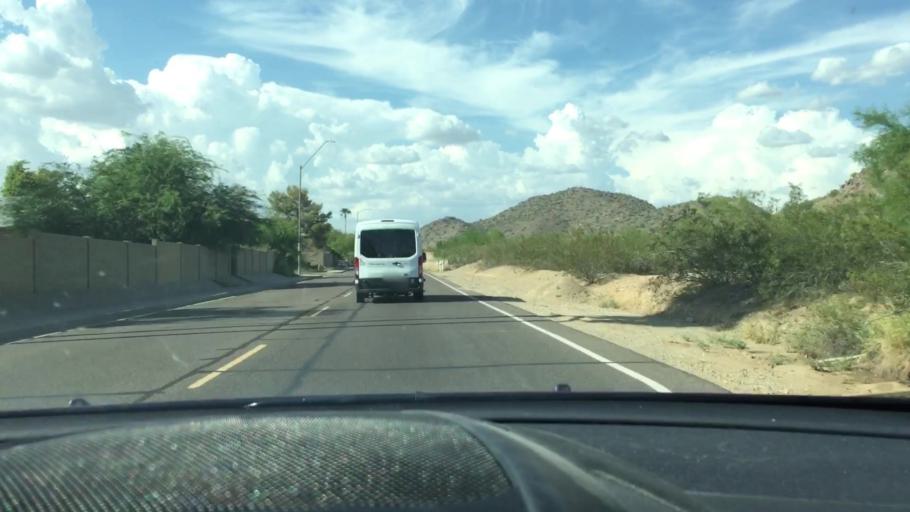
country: US
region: Arizona
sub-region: Maricopa County
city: Paradise Valley
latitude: 33.6629
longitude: -112.0485
